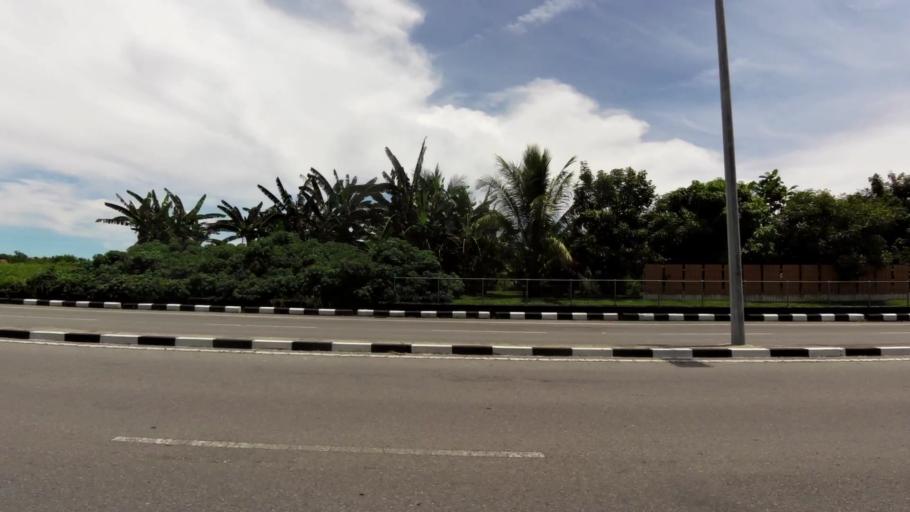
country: BN
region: Belait
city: Kuala Belait
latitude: 4.5861
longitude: 114.2460
